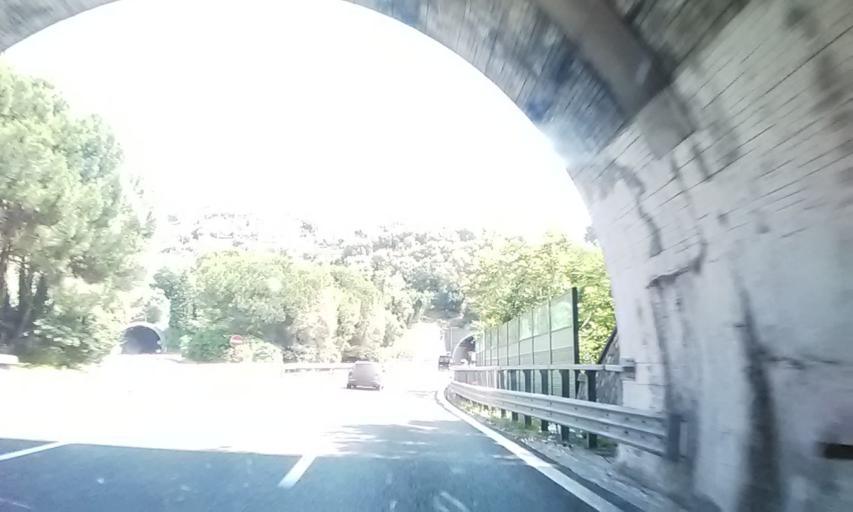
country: IT
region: Liguria
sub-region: Provincia di Savona
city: Celle Ligure
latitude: 44.3592
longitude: 8.5650
